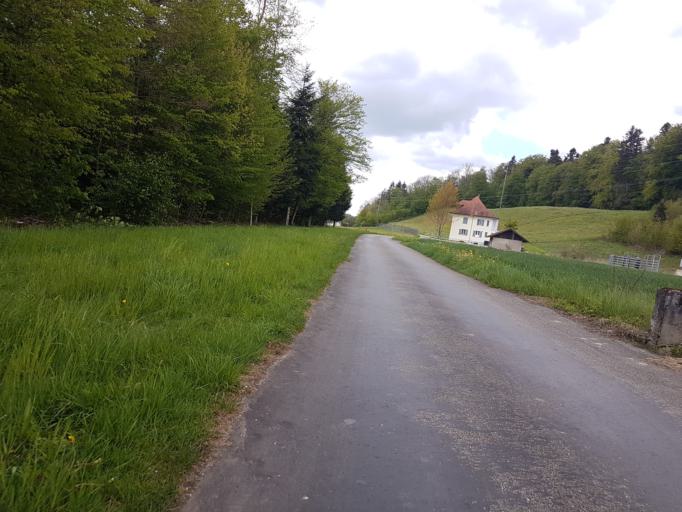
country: CH
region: Solothurn
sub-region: Bezirk Gaeu
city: Wolfwil
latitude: 47.2583
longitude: 7.7860
